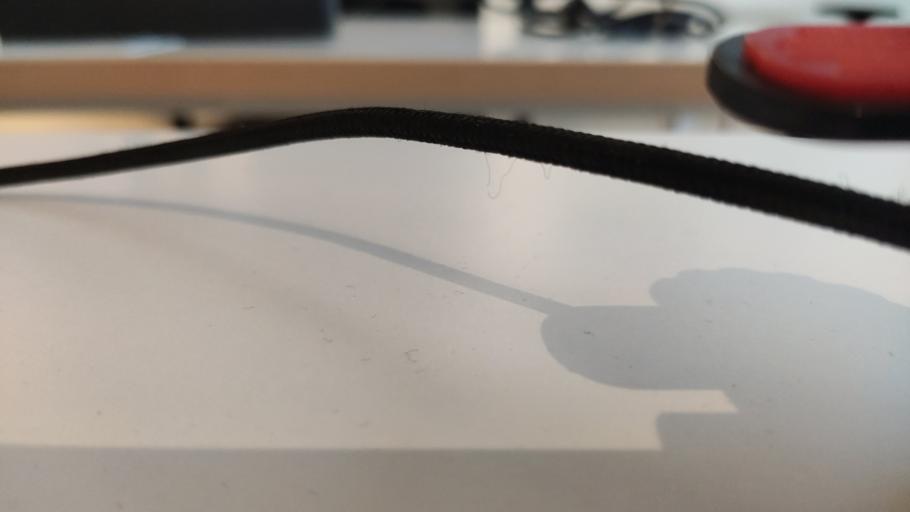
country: RU
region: Moskovskaya
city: Novopetrovskoye
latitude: 55.9630
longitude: 36.4400
